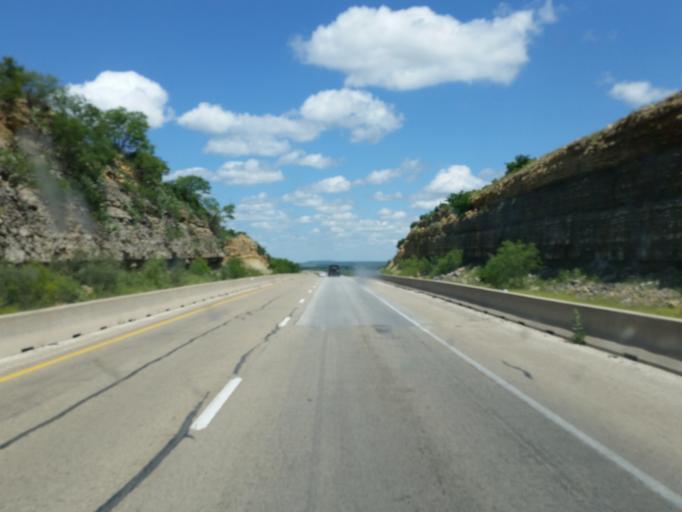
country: US
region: Texas
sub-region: Callahan County
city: Baird
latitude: 32.3951
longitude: -99.3626
